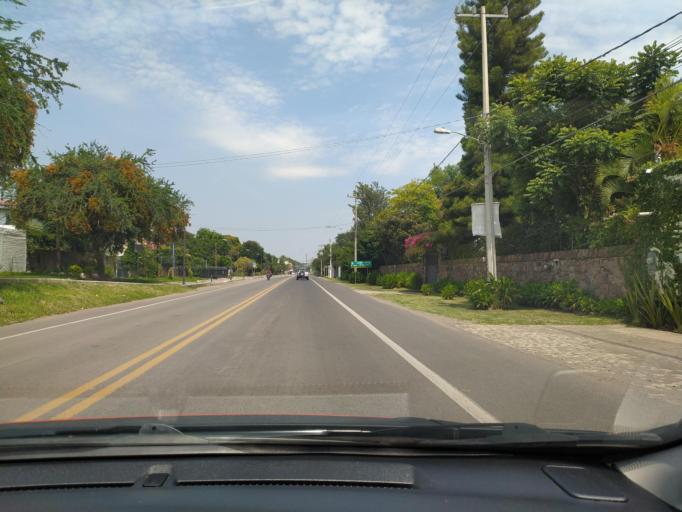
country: MX
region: Jalisco
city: San Juan Cosala
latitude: 20.2897
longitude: -103.3518
